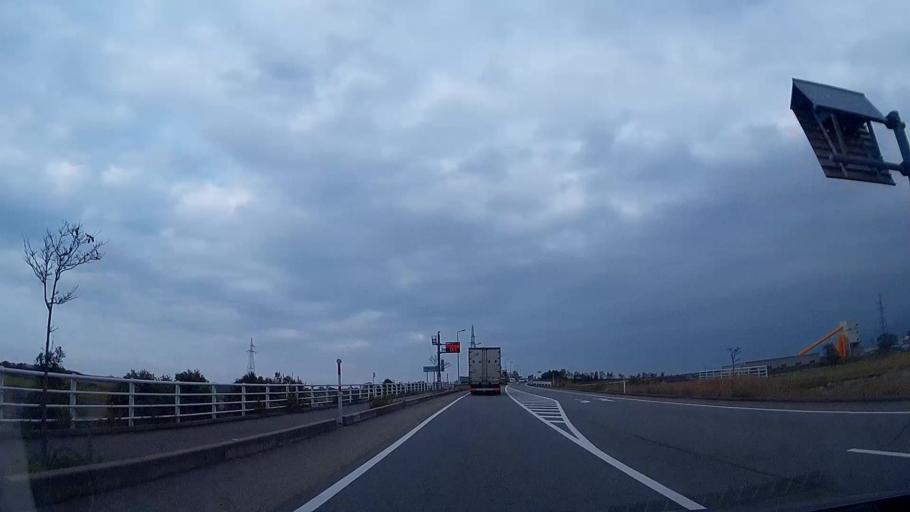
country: JP
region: Toyama
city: Nyuzen
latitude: 36.8998
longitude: 137.4461
